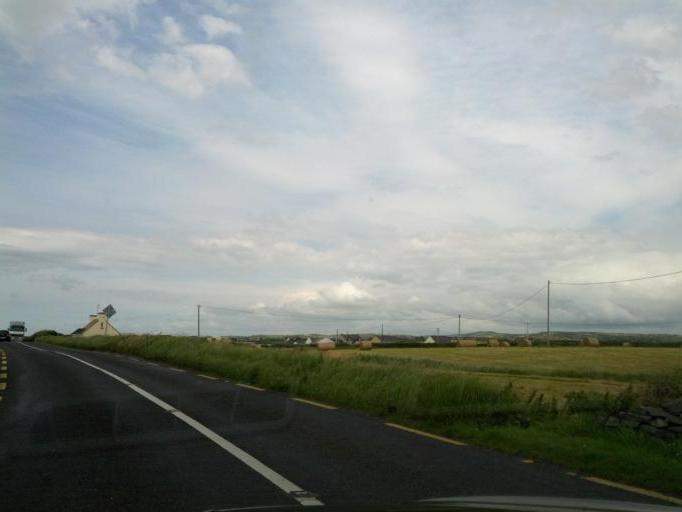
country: IE
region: Munster
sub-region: An Clar
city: Kilrush
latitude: 52.8328
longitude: -9.4310
